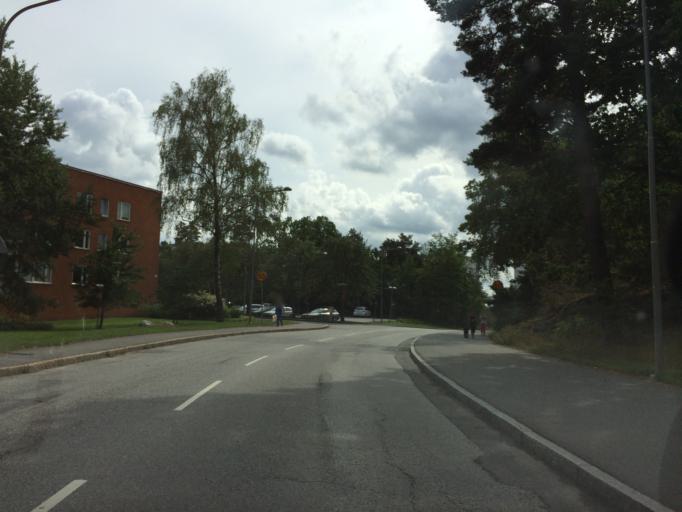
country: SE
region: Stockholm
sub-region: Stockholms Kommun
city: Arsta
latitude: 59.2844
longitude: 18.0119
